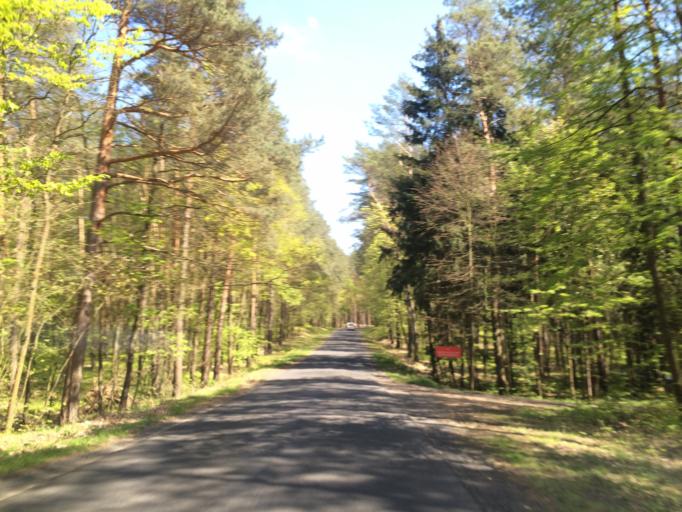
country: PL
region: Warmian-Masurian Voivodeship
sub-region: Powiat nowomiejski
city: Biskupiec
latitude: 53.3851
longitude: 19.3932
